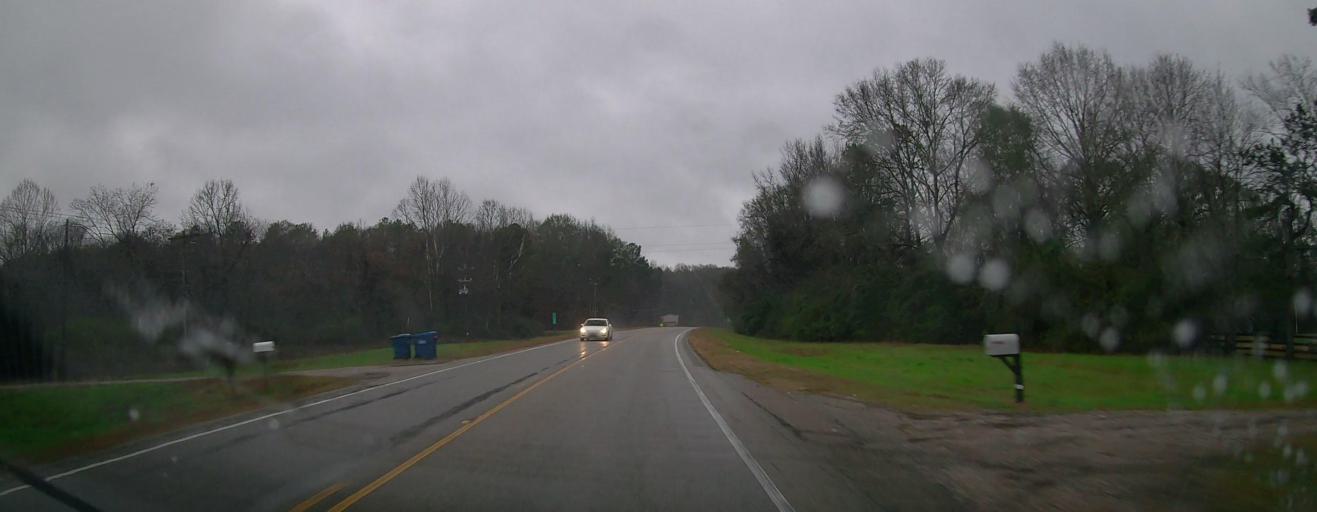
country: US
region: Alabama
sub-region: Autauga County
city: Prattville
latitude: 32.4977
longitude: -86.5817
